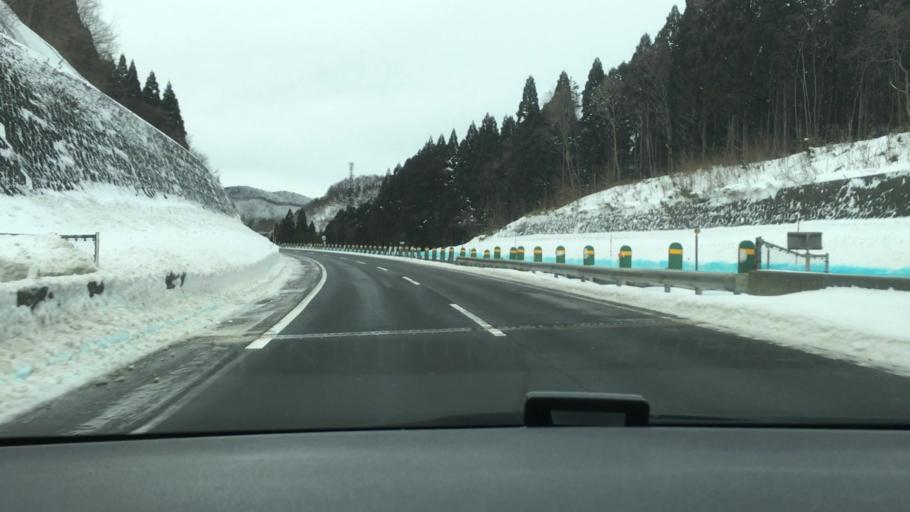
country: JP
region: Akita
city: Hanawa
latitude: 40.1201
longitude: 140.8520
